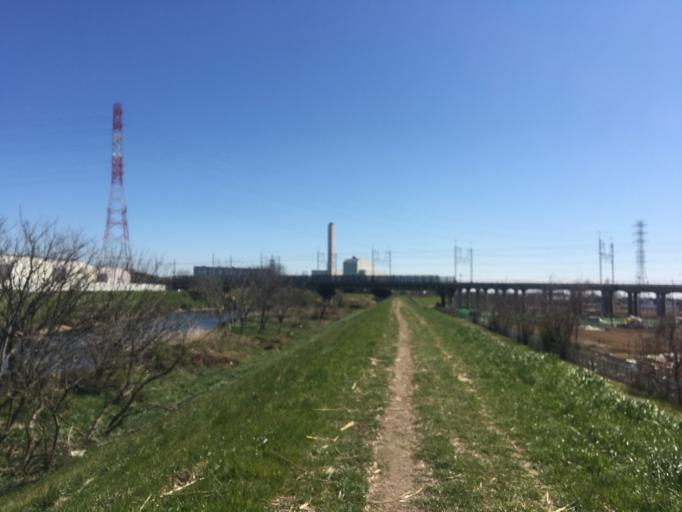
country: JP
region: Saitama
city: Shiki
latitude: 35.8243
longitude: 139.6003
